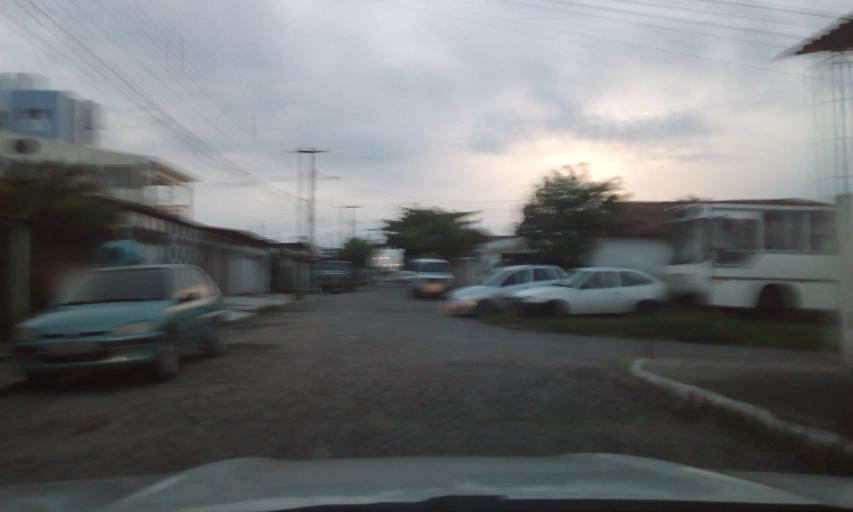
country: BR
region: Paraiba
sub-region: Joao Pessoa
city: Joao Pessoa
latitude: -7.1396
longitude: -34.8805
